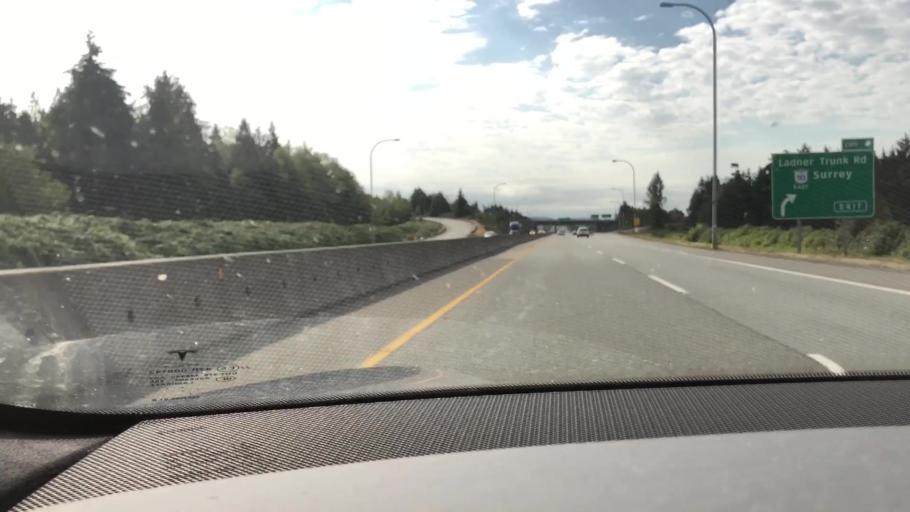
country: CA
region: British Columbia
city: Delta
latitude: 49.1071
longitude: -122.9032
